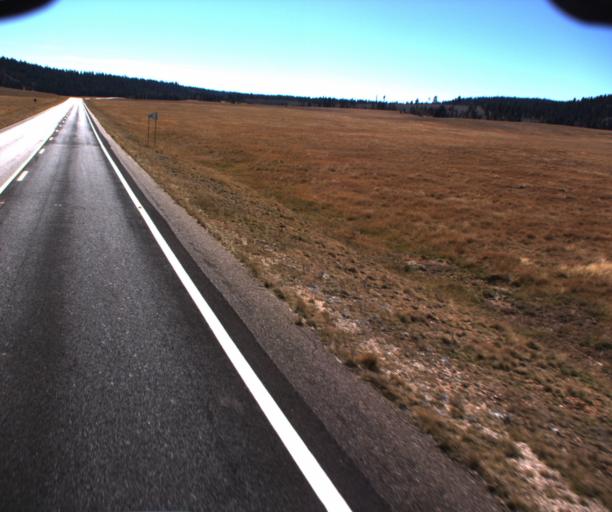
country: US
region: Arizona
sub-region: Coconino County
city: Grand Canyon
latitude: 36.4868
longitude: -112.1293
